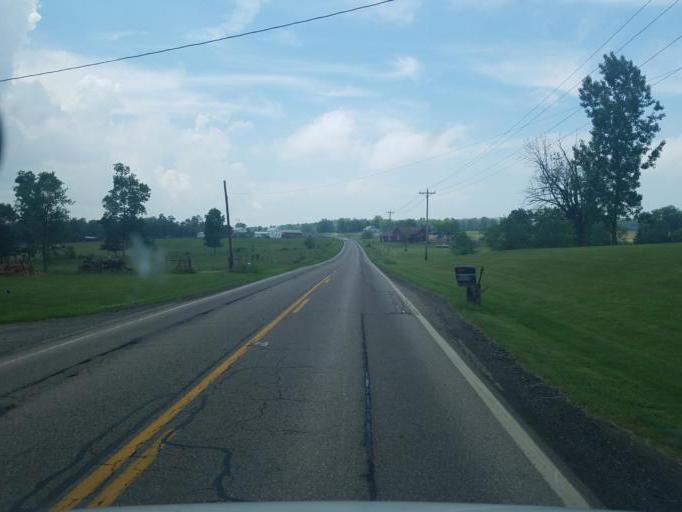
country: US
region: Ohio
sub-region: Knox County
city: Oak Hill
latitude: 40.3404
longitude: -82.2663
